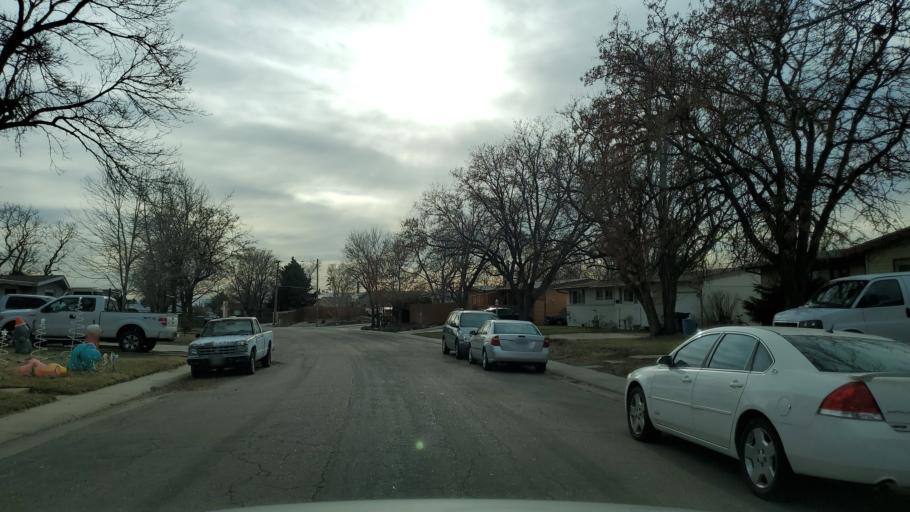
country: US
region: Colorado
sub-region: Adams County
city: Westminster
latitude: 39.8400
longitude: -105.0214
